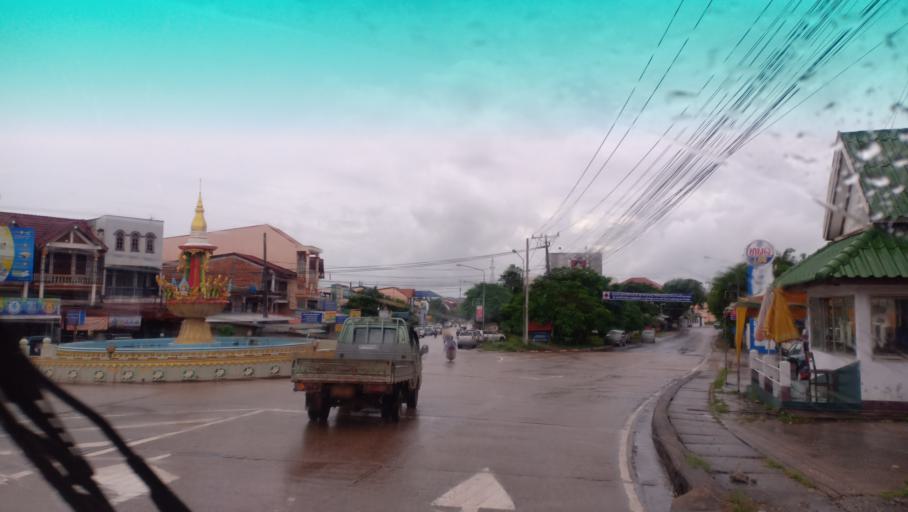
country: LA
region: Khammouan
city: Thakhek
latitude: 17.4009
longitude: 104.8217
